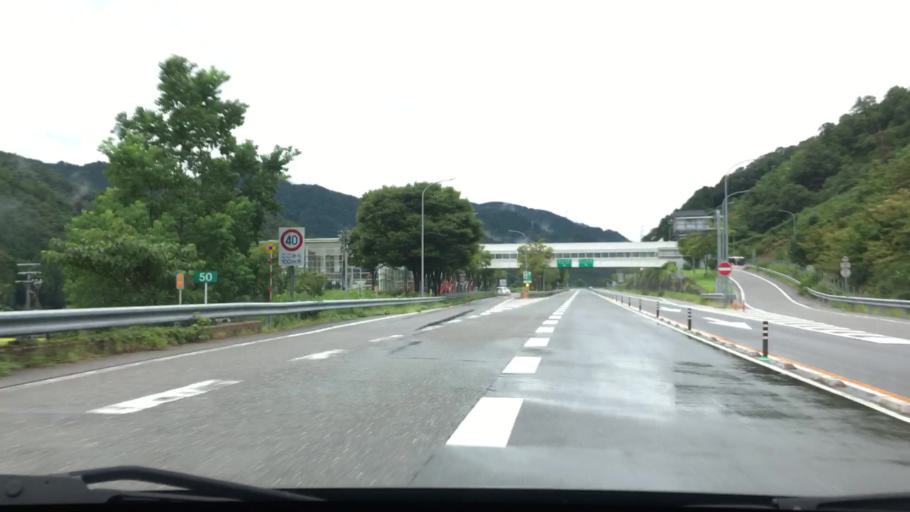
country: JP
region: Hyogo
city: Nishiwaki
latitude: 35.2148
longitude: 134.7937
